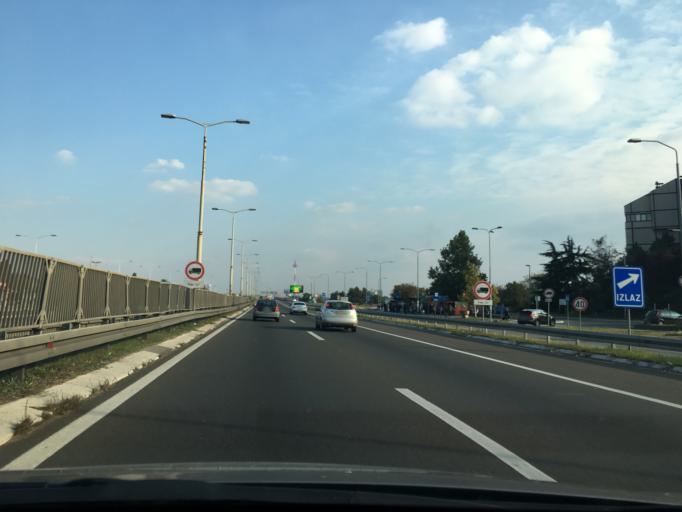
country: RS
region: Central Serbia
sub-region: Belgrade
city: Novi Beograd
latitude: 44.8080
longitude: 20.4299
